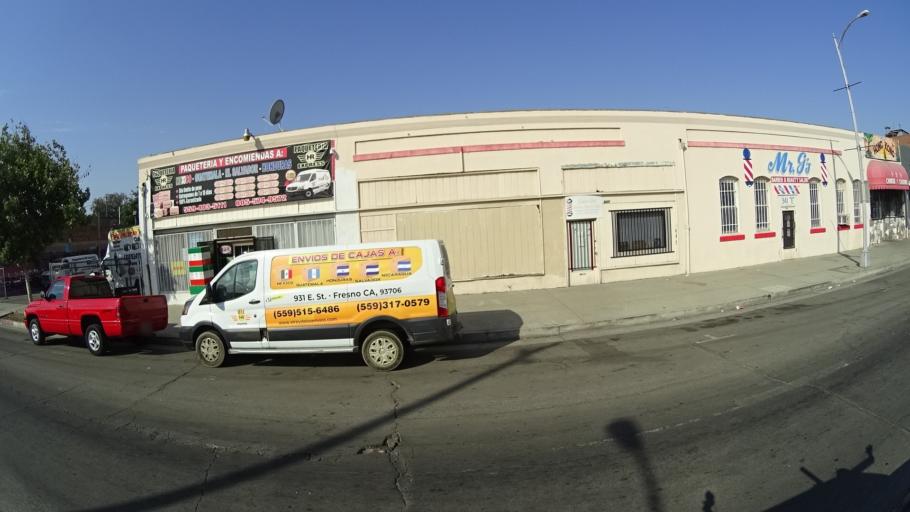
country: US
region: California
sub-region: Fresno County
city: Fresno
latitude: 36.7294
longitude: -119.7955
